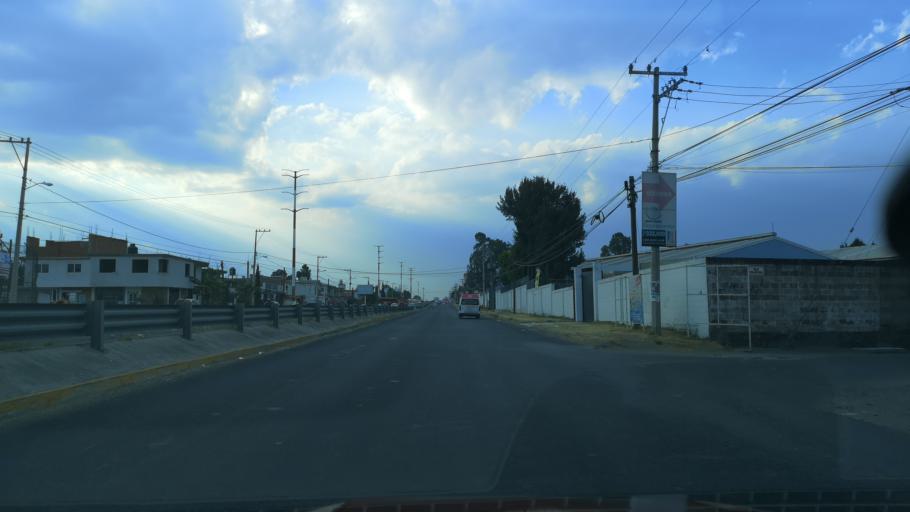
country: MX
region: Puebla
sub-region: Juan C. Bonilla
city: Santa Maria Zacatepec
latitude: 19.1097
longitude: -98.3534
